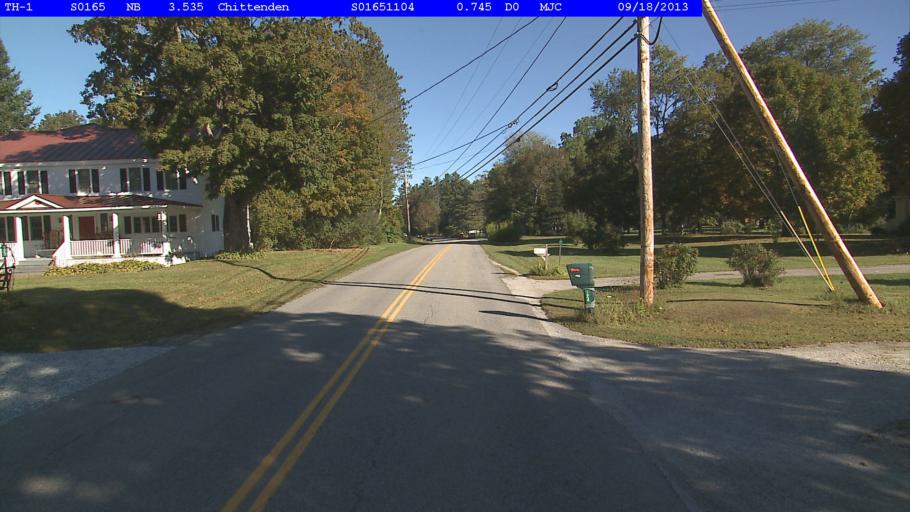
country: US
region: Vermont
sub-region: Rutland County
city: Rutland
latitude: 43.6876
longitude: -72.9515
